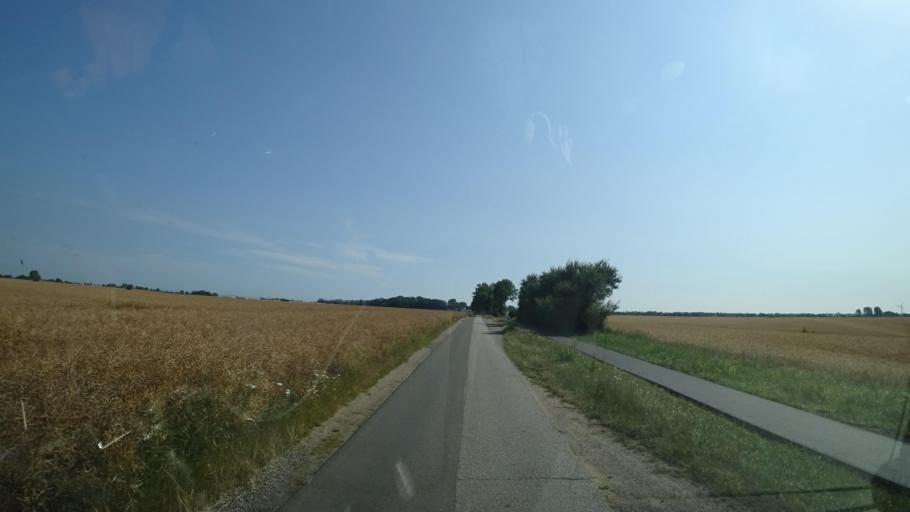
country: DE
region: Mecklenburg-Vorpommern
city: Kemnitz
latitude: 54.1149
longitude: 13.5350
